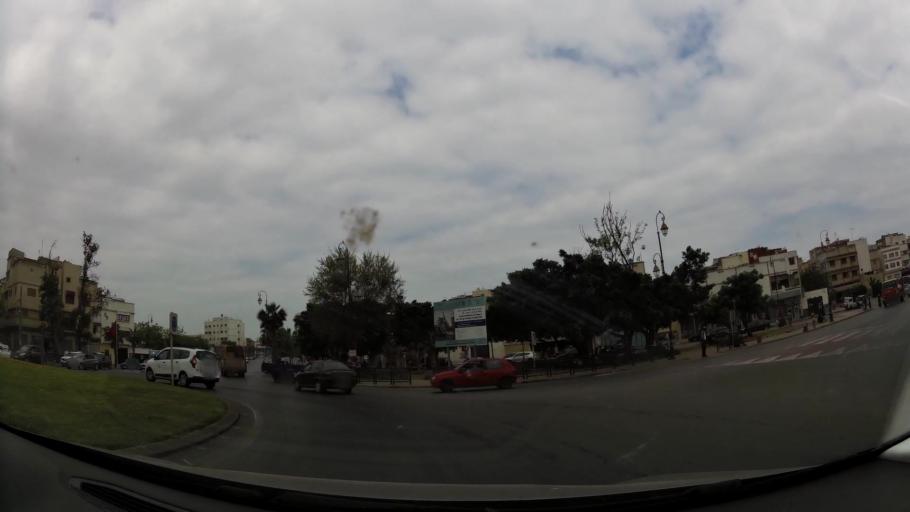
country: MA
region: Rabat-Sale-Zemmour-Zaer
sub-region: Rabat
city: Rabat
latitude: 33.9912
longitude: -6.8710
